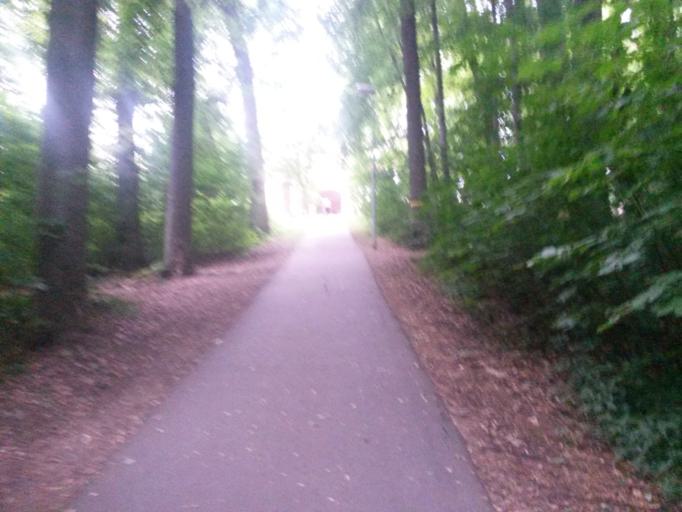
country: DE
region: Bavaria
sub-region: Upper Palatinate
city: Amberg
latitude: 49.4517
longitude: 11.8728
